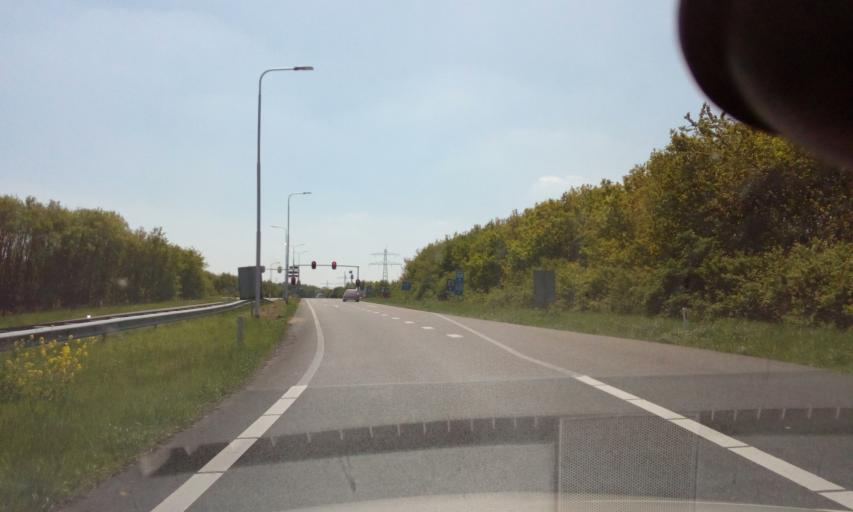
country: NL
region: North Brabant
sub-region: Gemeente Cuijk
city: Cuijk
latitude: 51.7714
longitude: 5.8349
